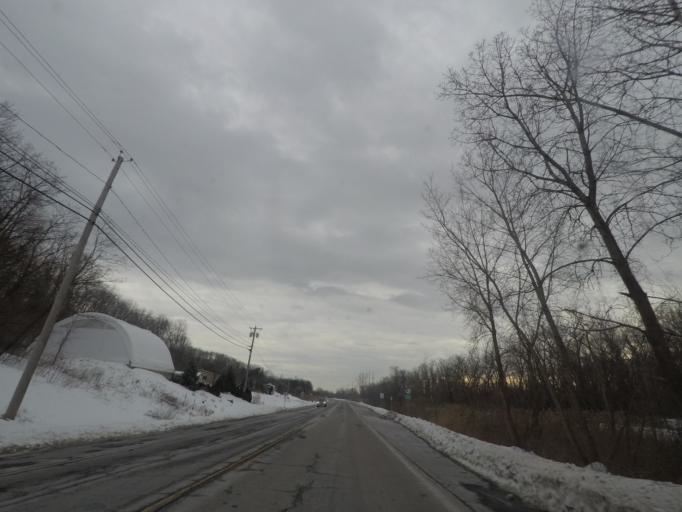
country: US
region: New York
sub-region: Rensselaer County
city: Hampton Manor
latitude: 42.6180
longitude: -73.7463
